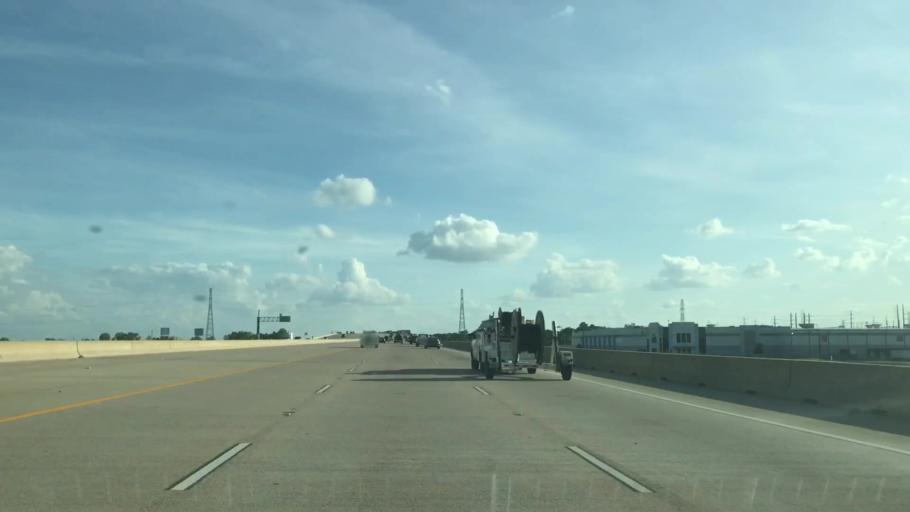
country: US
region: Texas
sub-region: Tarrant County
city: Euless
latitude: 32.8229
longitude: -97.0178
